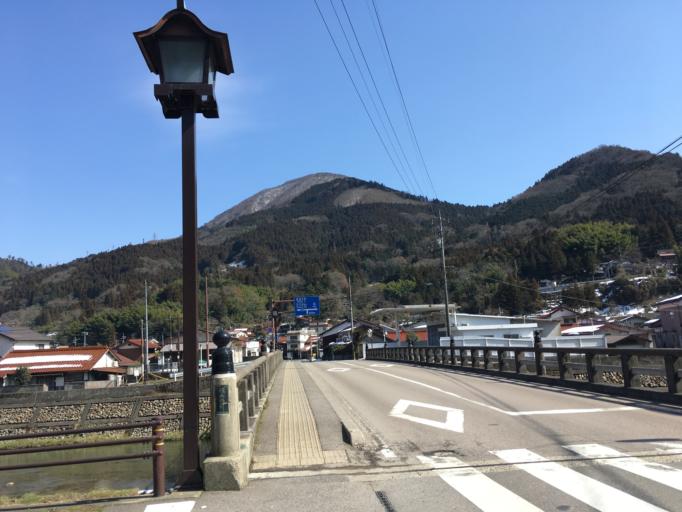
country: JP
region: Shimane
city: Masuda
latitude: 34.4624
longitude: 131.7698
